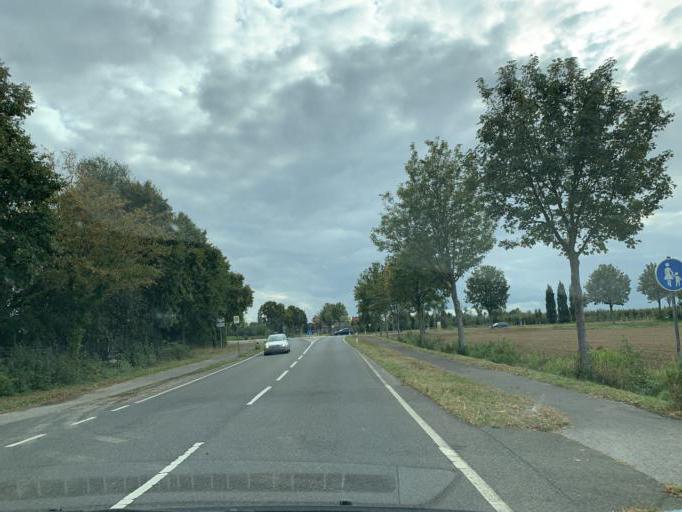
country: DE
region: North Rhine-Westphalia
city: Huckelhoven
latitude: 51.0931
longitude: 6.2632
